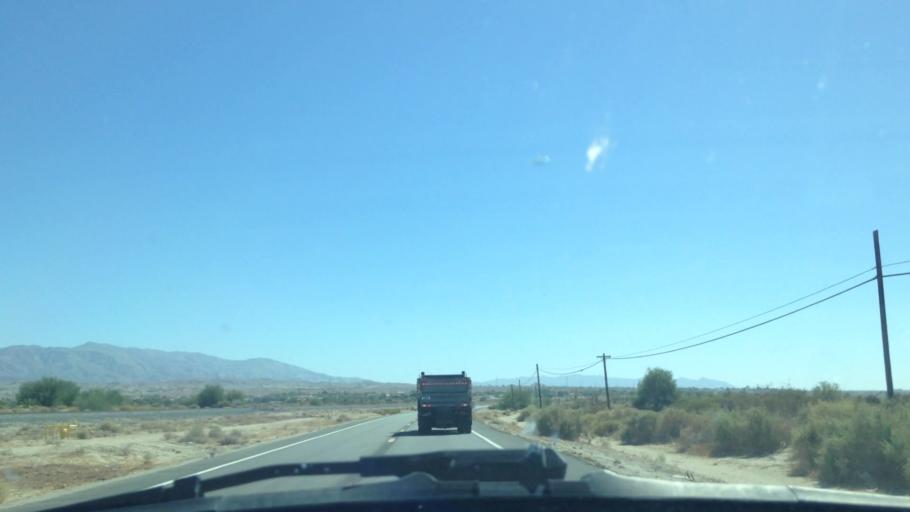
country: US
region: California
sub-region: Riverside County
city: Mecca
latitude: 33.5325
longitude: -115.9545
